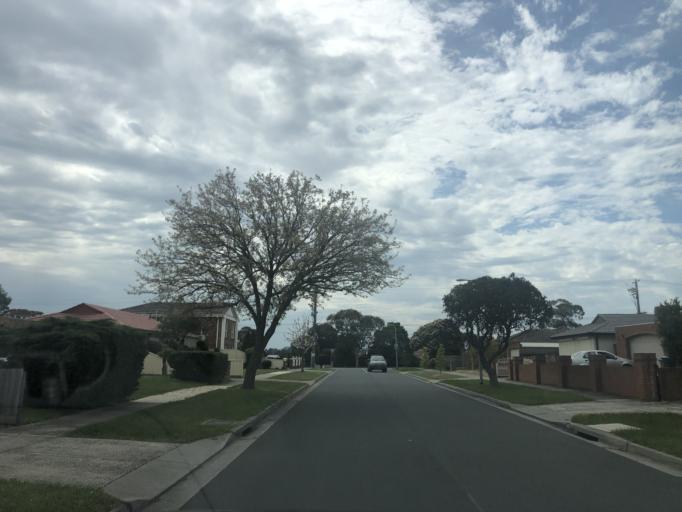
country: AU
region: Victoria
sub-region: Casey
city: Hallam
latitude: -38.0012
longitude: 145.2636
